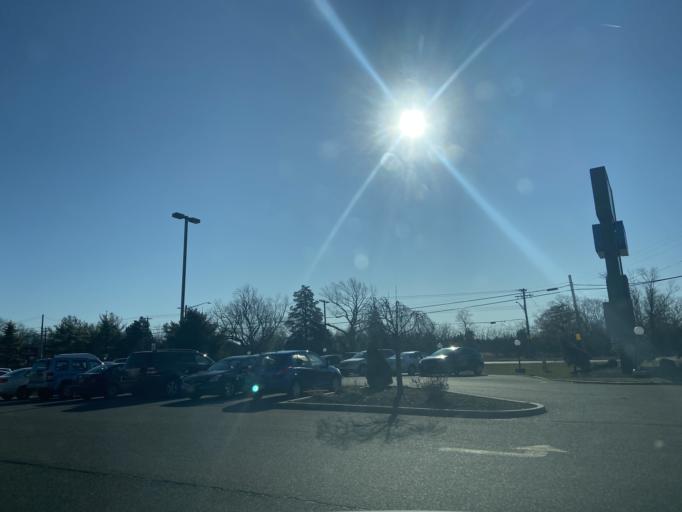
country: US
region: New Jersey
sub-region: Cumberland County
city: Vineland
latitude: 39.4887
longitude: -75.0687
